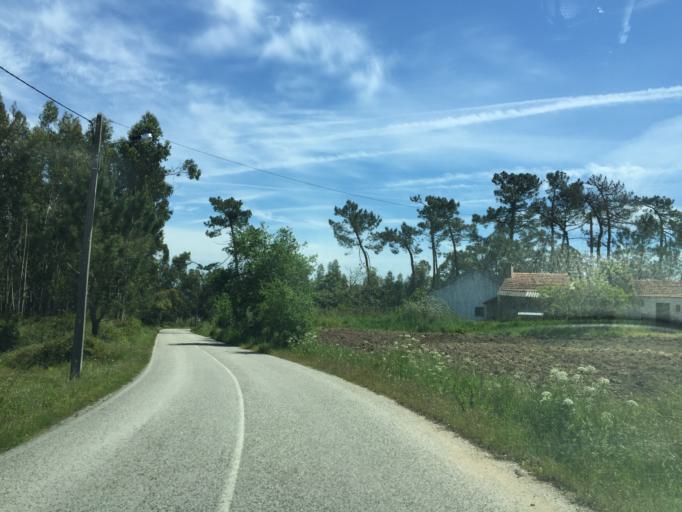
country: PT
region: Coimbra
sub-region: Figueira da Foz
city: Lavos
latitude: 40.0702
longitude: -8.7683
